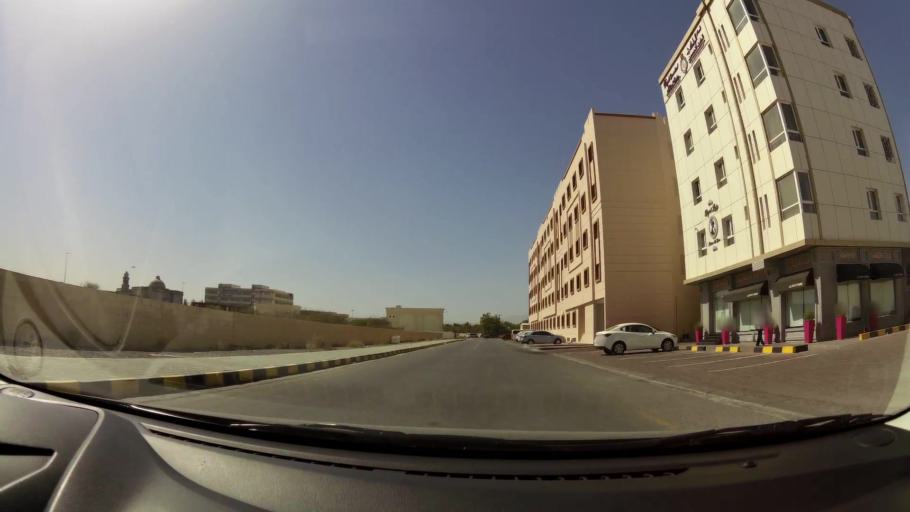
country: OM
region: Muhafazat Masqat
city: As Sib al Jadidah
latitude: 23.6101
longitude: 58.2440
